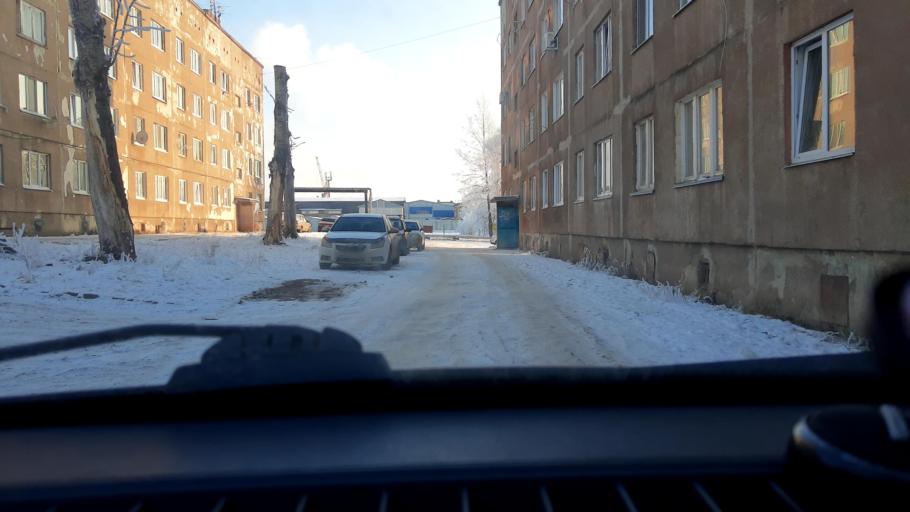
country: RU
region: Bashkortostan
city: Iglino
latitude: 54.7718
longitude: 56.2403
